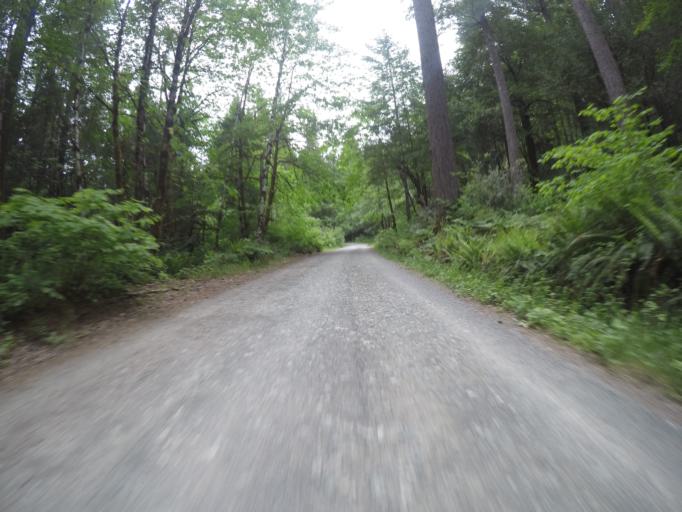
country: US
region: California
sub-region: Del Norte County
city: Bertsch-Oceanview
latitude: 41.6887
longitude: -123.9065
